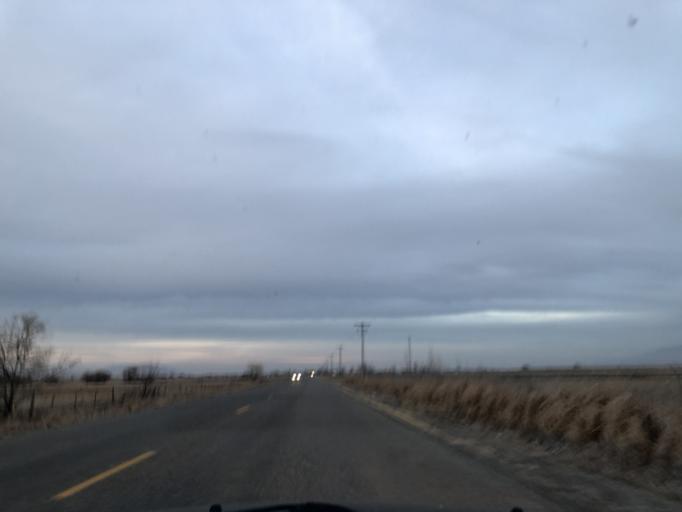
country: US
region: Utah
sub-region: Cache County
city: Benson
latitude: 41.7667
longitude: -111.9117
